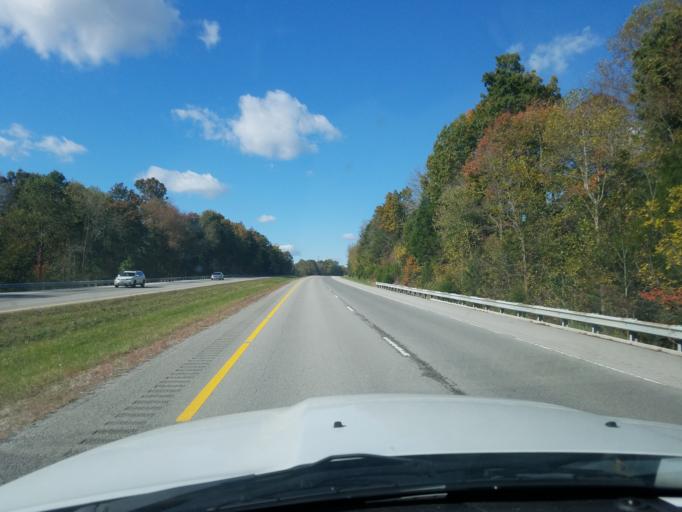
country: US
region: Kentucky
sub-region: Metcalfe County
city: Edmonton
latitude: 36.9956
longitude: -85.7522
